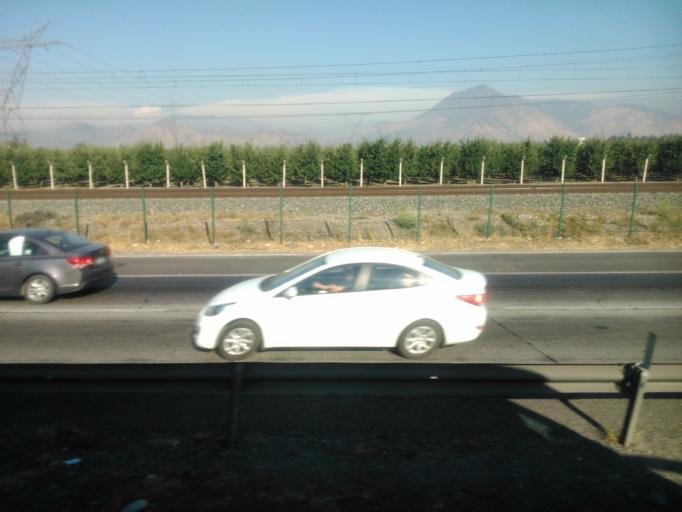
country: CL
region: Santiago Metropolitan
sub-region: Provincia de Maipo
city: Buin
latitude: -33.7016
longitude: -70.7224
